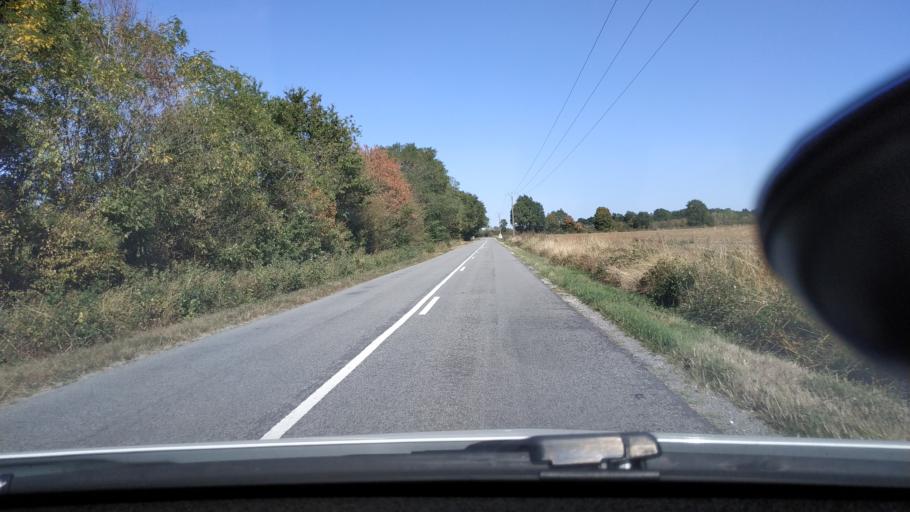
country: FR
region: Centre
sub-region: Departement du Loiret
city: Coullons
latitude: 47.6318
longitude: 2.5120
